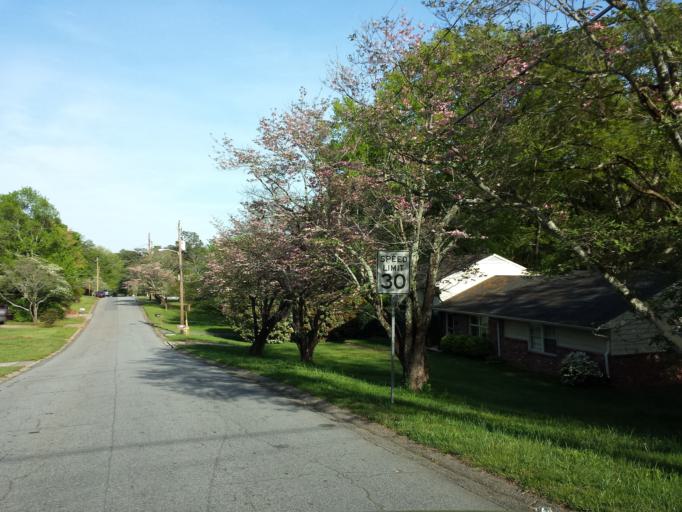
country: US
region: Georgia
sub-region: Cobb County
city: Marietta
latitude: 33.9698
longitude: -84.5478
